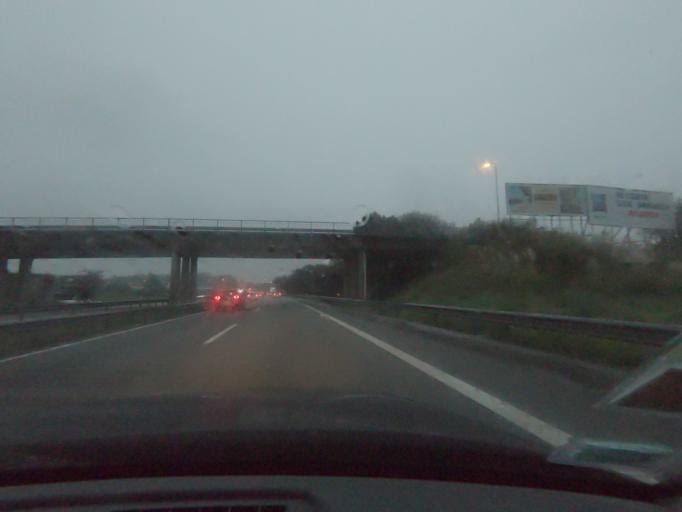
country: PT
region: Porto
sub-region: Matosinhos
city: Lavra
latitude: 41.2541
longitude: -8.7004
